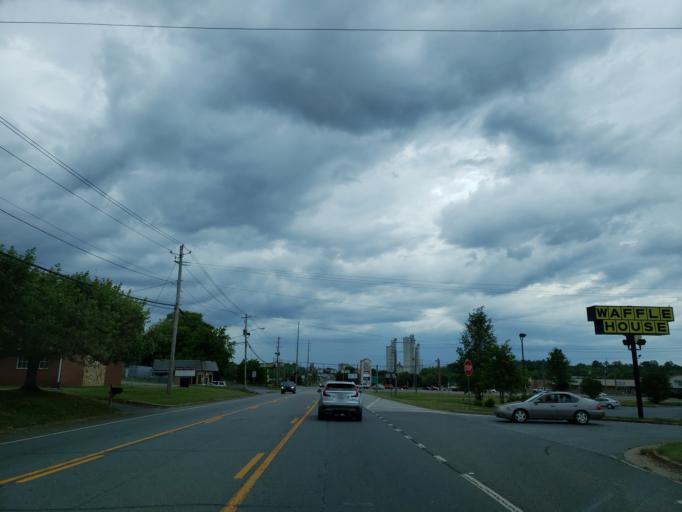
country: US
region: Georgia
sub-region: Polk County
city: Rockmart
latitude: 34.0093
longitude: -85.0430
